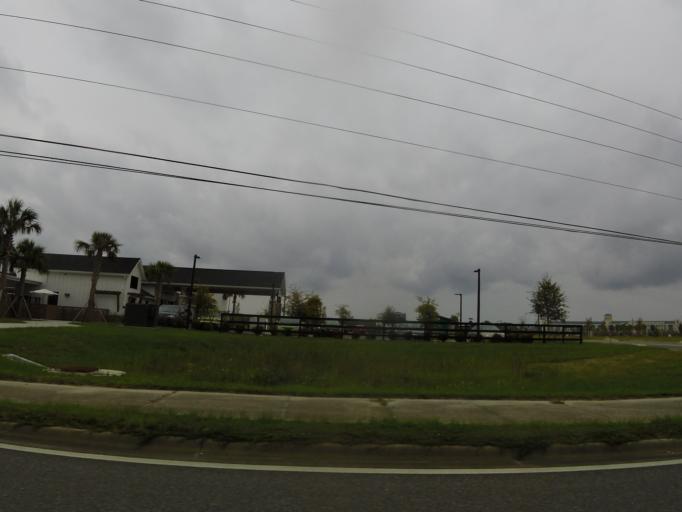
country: US
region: Florida
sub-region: Clay County
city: Middleburg
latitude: 30.1144
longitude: -81.8291
